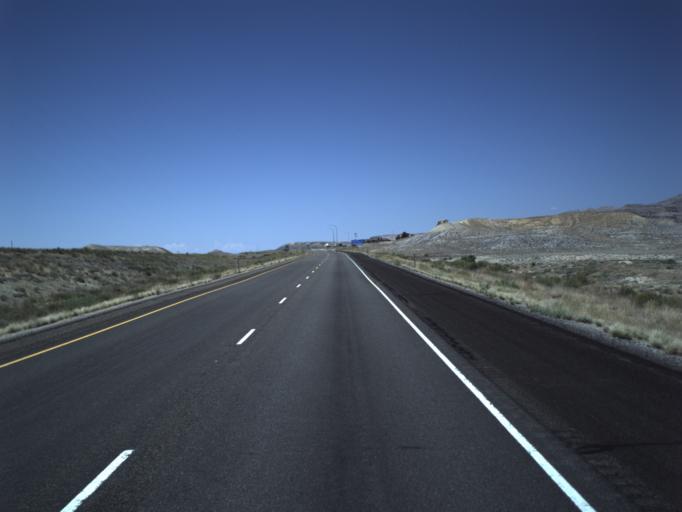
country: US
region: Utah
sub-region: Grand County
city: Moab
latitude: 38.9496
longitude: -109.6736
